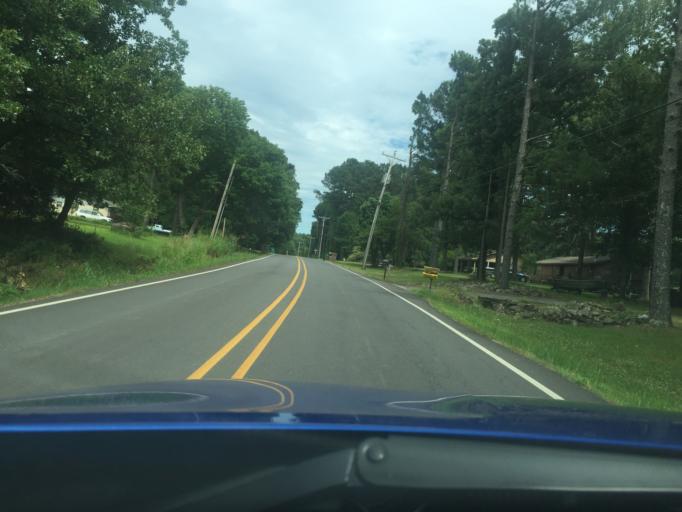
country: US
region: Arkansas
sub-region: Pulaski County
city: Maumelle
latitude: 34.8311
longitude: -92.4473
